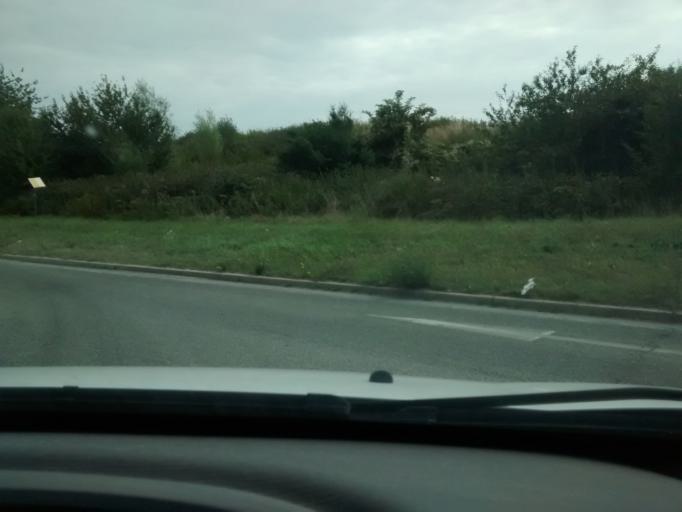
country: FR
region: Ile-de-France
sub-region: Departement des Yvelines
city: Buc
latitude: 48.7650
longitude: 2.1278
